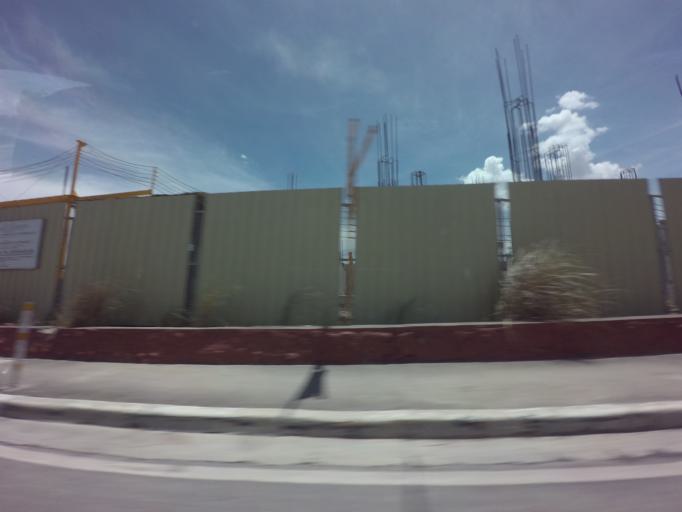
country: PH
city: Sambayanihan People's Village
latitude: 14.4883
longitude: 120.9995
